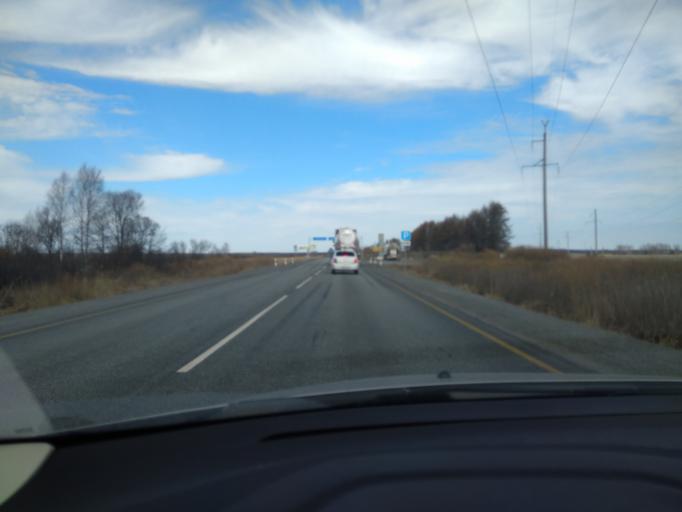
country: RU
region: Sverdlovsk
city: Pyshma
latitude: 57.0278
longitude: 63.4074
